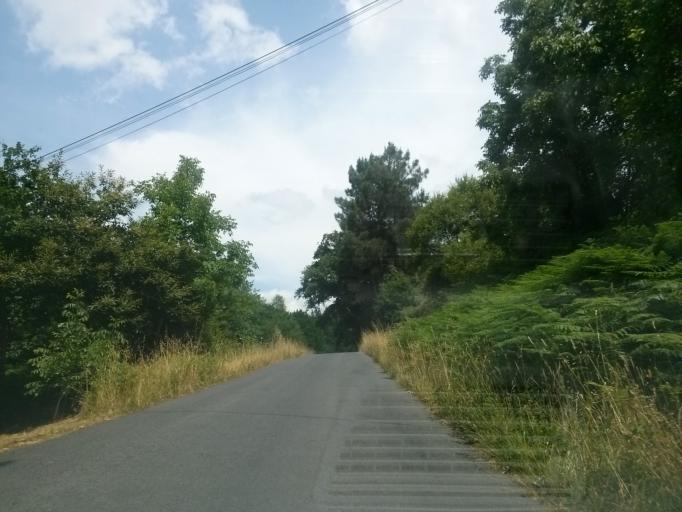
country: ES
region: Galicia
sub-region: Provincia de Lugo
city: Lugo
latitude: 43.0334
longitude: -7.5876
